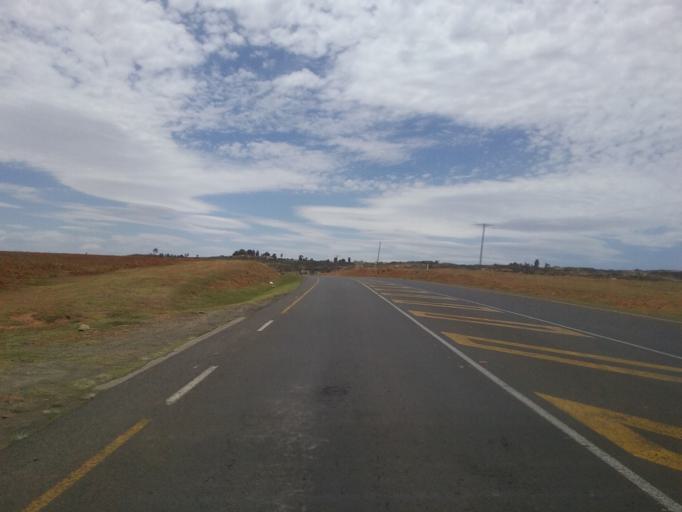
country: LS
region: Maseru
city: Maseru
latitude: -29.5065
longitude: 27.5267
